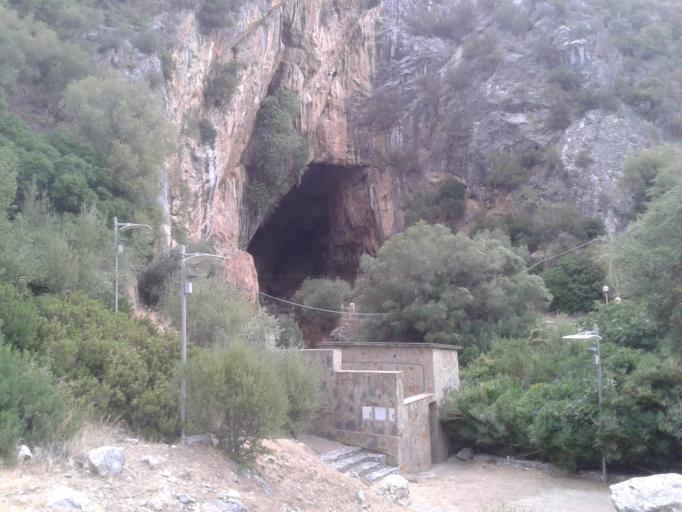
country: IT
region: Sardinia
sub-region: Provincia di Carbonia-Iglesias
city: Domusnovas
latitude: 39.3367
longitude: 8.6271
